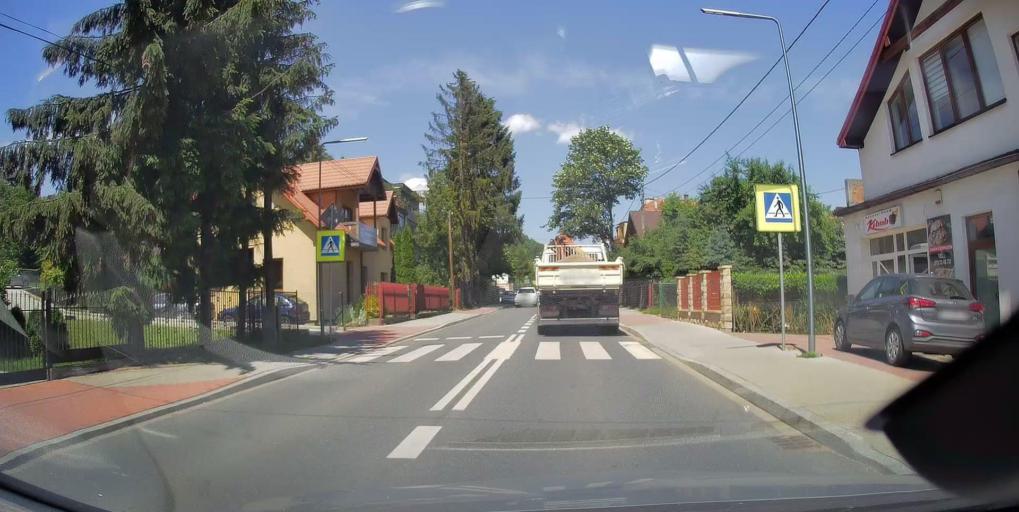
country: PL
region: Lesser Poland Voivodeship
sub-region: Powiat nowosadecki
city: Krynica-Zdroj
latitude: 49.4037
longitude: 20.9532
